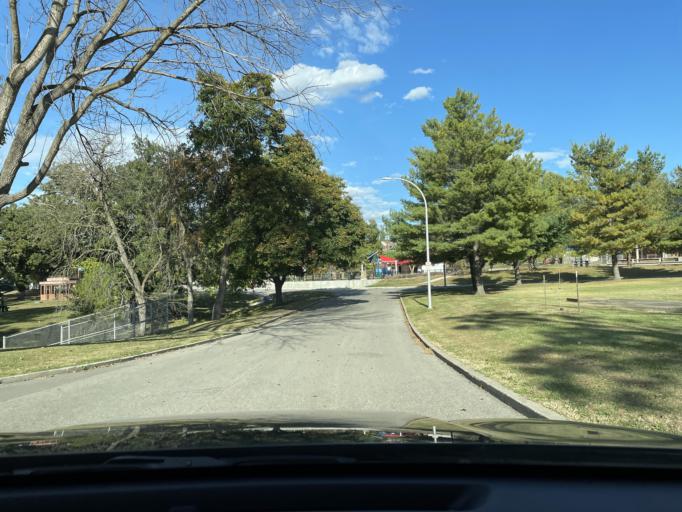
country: US
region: Kansas
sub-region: Doniphan County
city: Elwood
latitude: 39.7095
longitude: -94.8513
